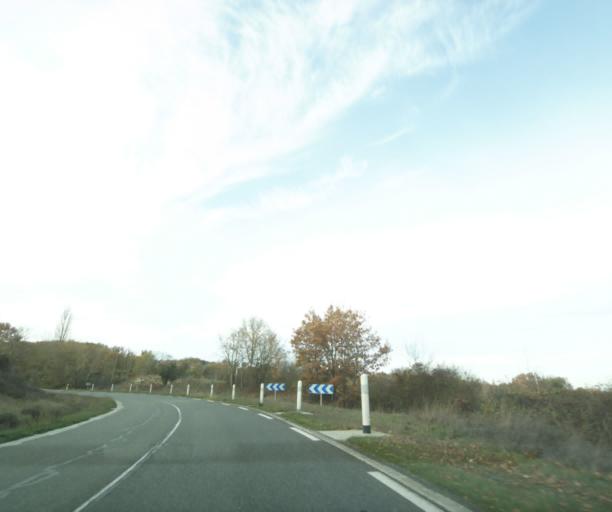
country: FR
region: Midi-Pyrenees
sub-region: Departement du Gers
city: Vic-Fezensac
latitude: 43.7361
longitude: 0.3730
